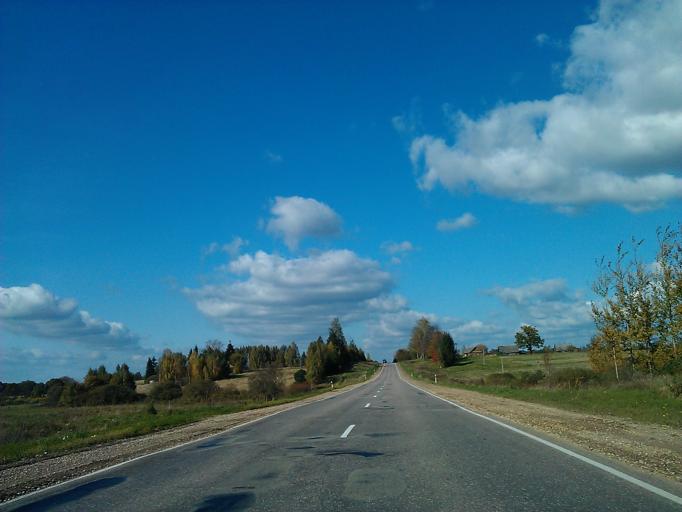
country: LV
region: Varkava
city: Vecvarkava
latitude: 56.1658
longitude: 26.3279
